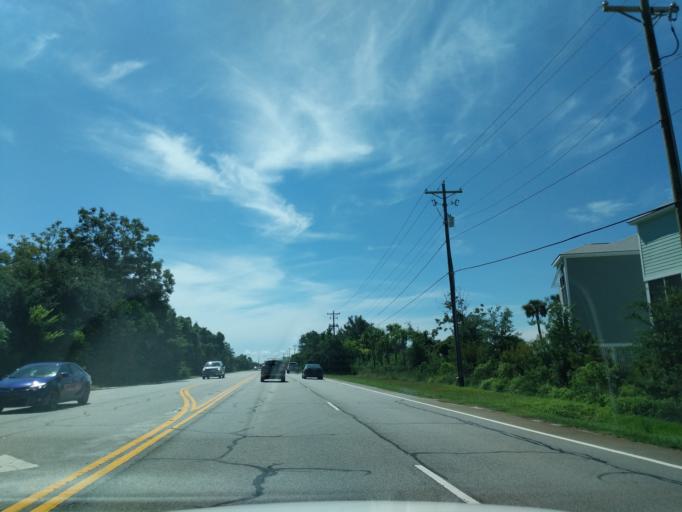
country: US
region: South Carolina
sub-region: Charleston County
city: Folly Beach
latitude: 32.6852
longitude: -79.9593
